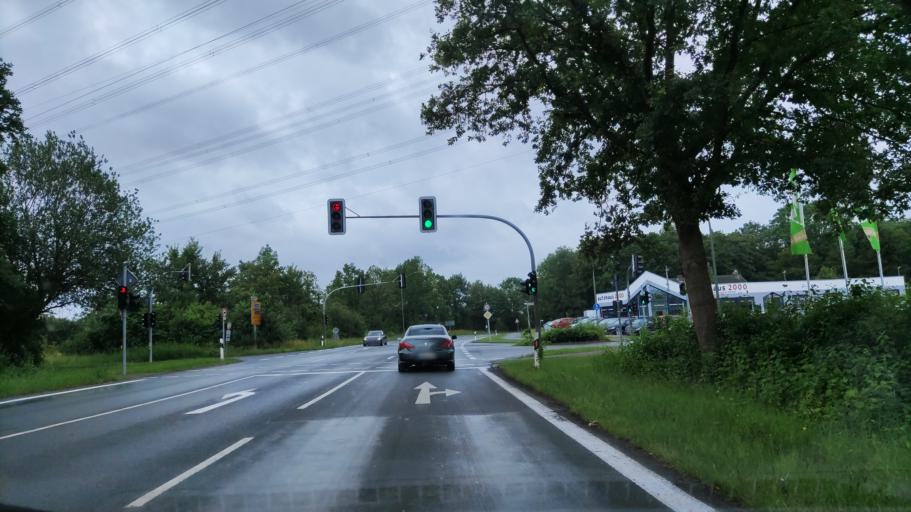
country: DE
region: North Rhine-Westphalia
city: Ahlen
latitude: 51.7367
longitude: 7.8808
